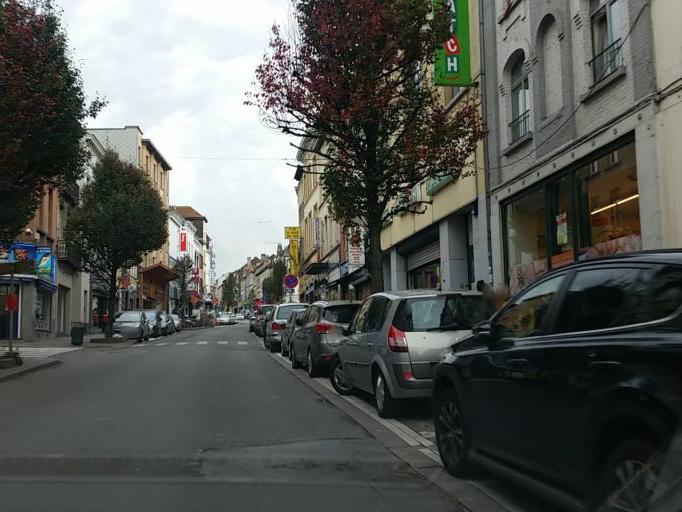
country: BE
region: Brussels Capital
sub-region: Bruxelles-Capitale
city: Brussels
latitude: 50.8300
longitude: 4.3444
